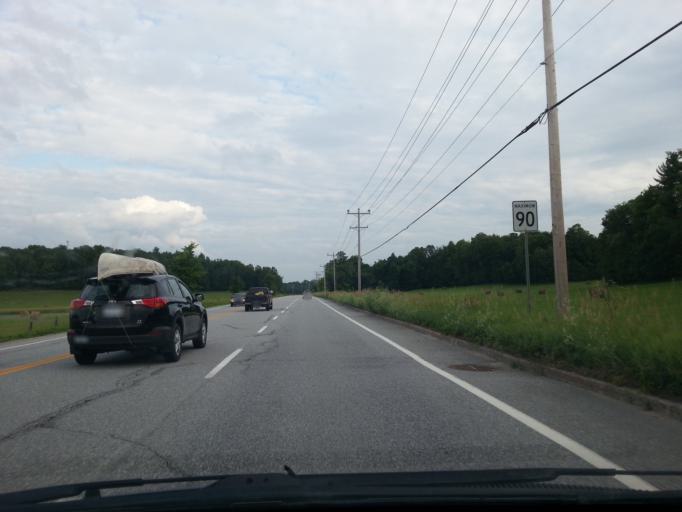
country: CA
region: Quebec
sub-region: Outaouais
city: Wakefield
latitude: 45.8376
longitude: -75.9735
